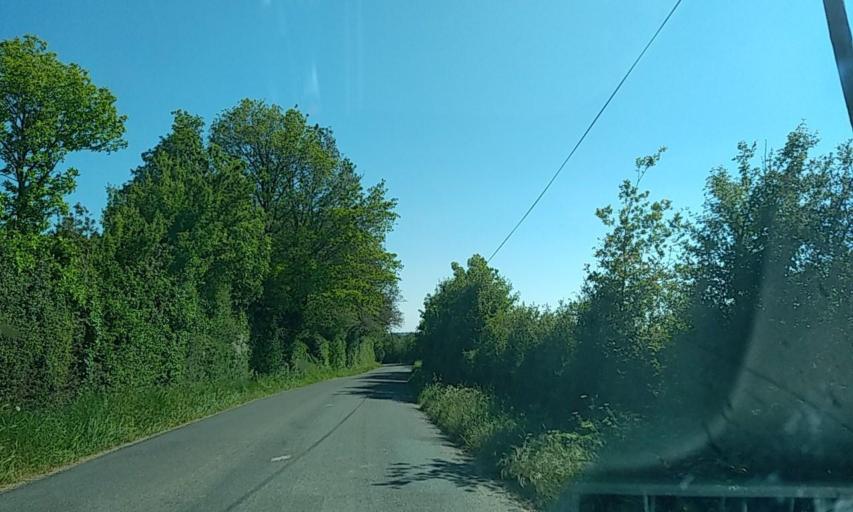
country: FR
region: Poitou-Charentes
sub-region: Departement des Deux-Sevres
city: Boisme
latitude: 46.7911
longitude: -0.4517
